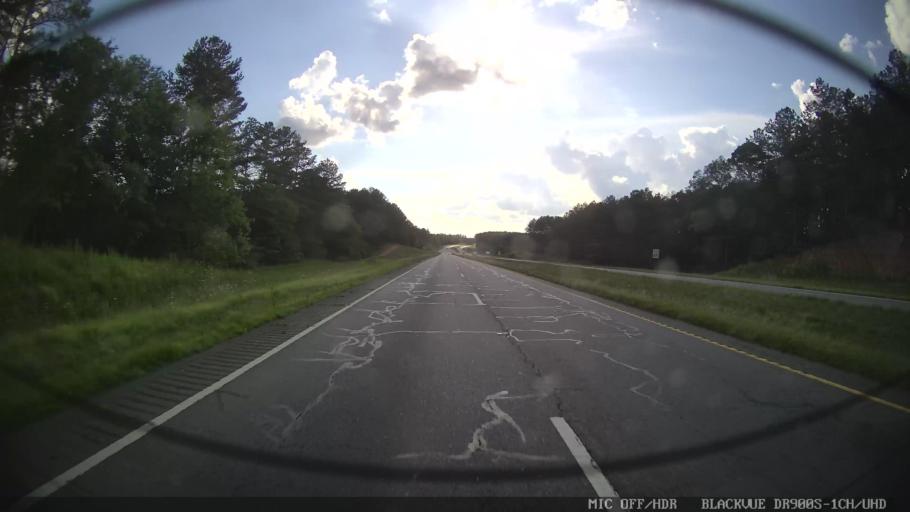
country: US
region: Georgia
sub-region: Bartow County
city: Euharlee
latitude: 34.2035
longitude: -85.0241
